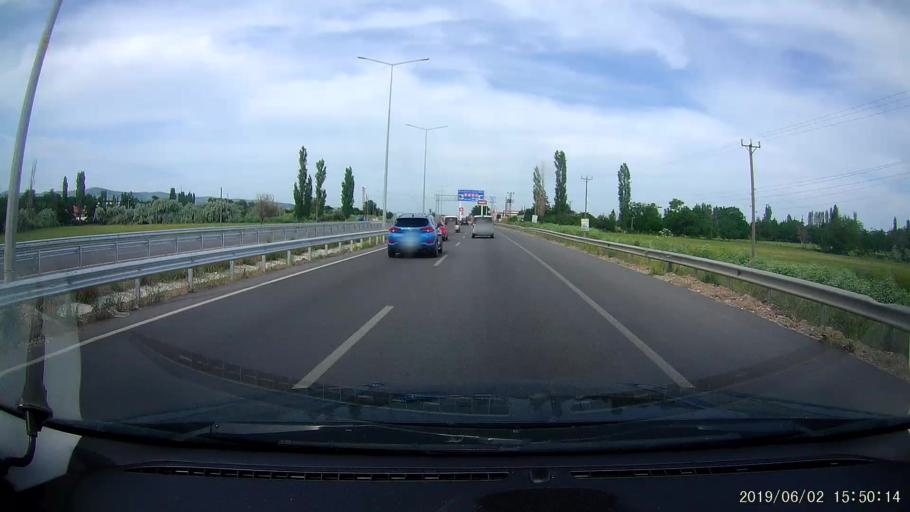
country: TR
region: Amasya
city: Merzifon
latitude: 40.8582
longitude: 35.4773
